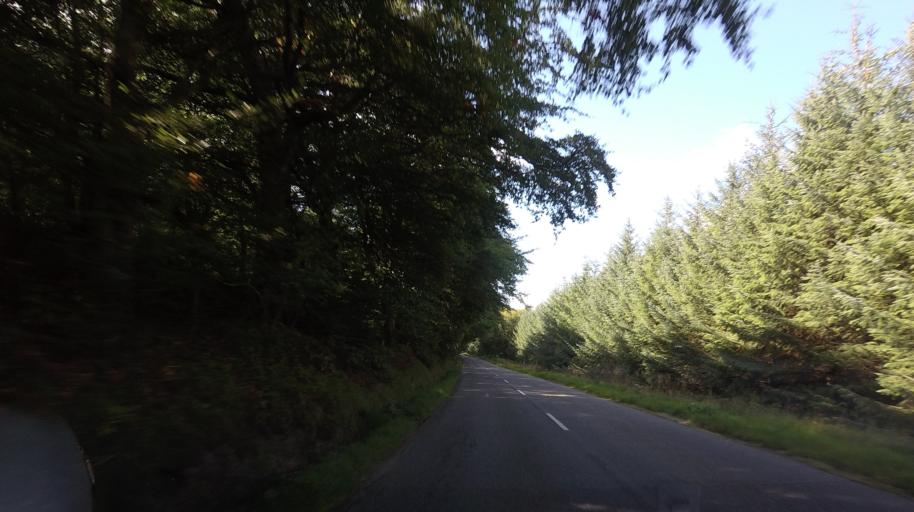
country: GB
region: Scotland
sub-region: Aberdeenshire
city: Alford
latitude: 57.1531
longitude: -2.7206
